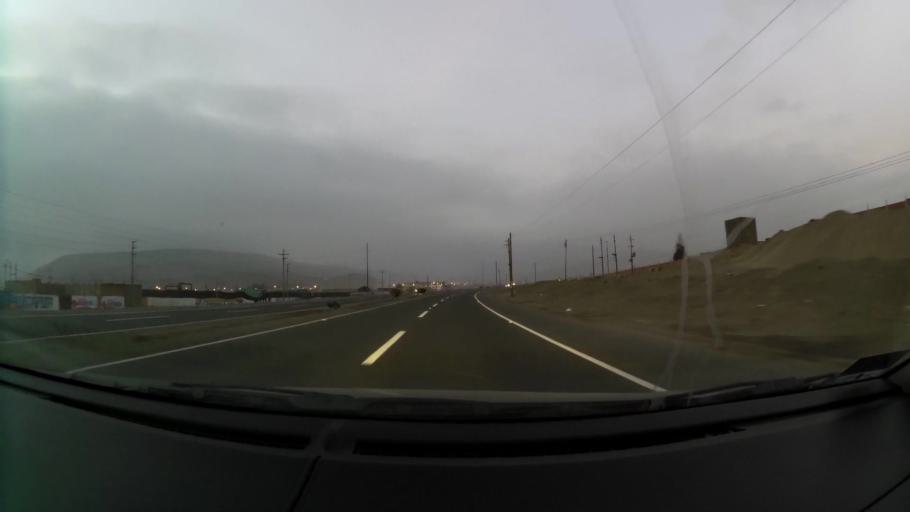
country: PE
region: Lima
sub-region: Lima
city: Santa Rosa
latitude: -11.7630
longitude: -77.1572
